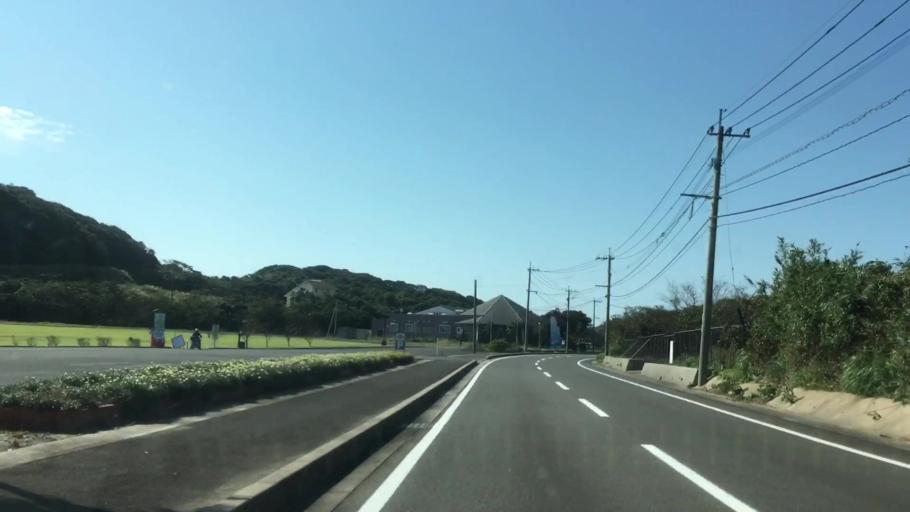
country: JP
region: Nagasaki
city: Sasebo
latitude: 33.0163
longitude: 129.5737
